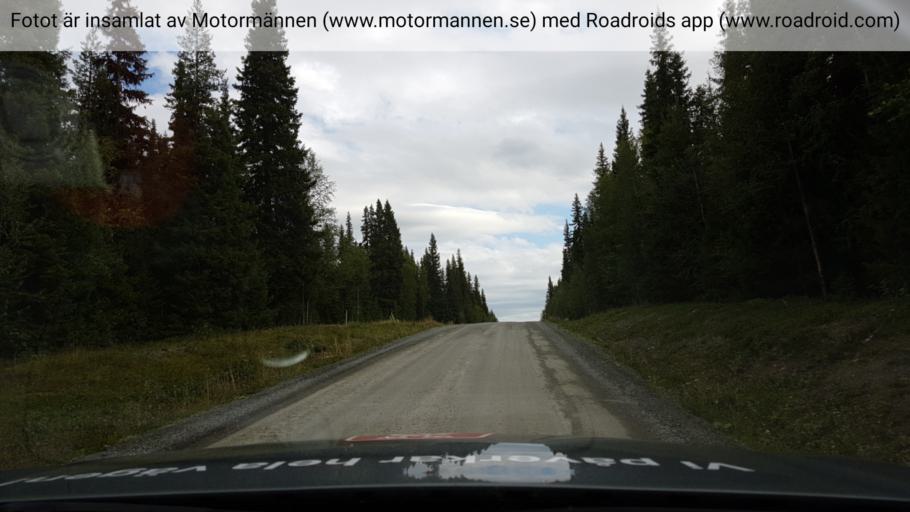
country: SE
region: Jaemtland
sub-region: Krokoms Kommun
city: Valla
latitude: 63.6616
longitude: 13.7561
